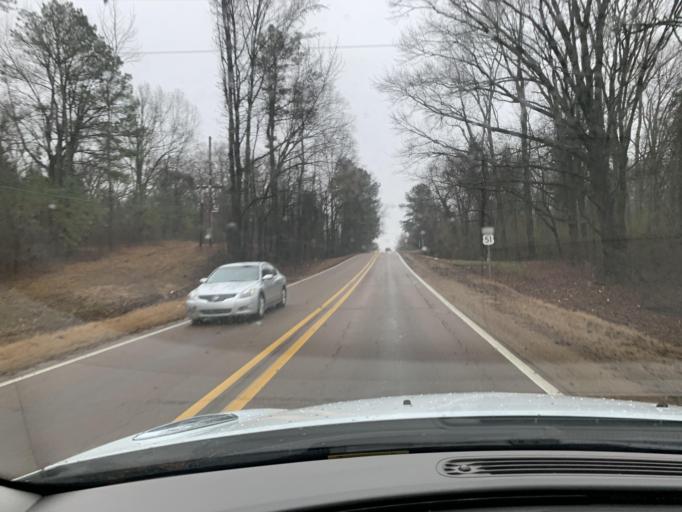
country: US
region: Mississippi
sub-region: De Soto County
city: Hernando
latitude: 34.8821
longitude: -89.9961
